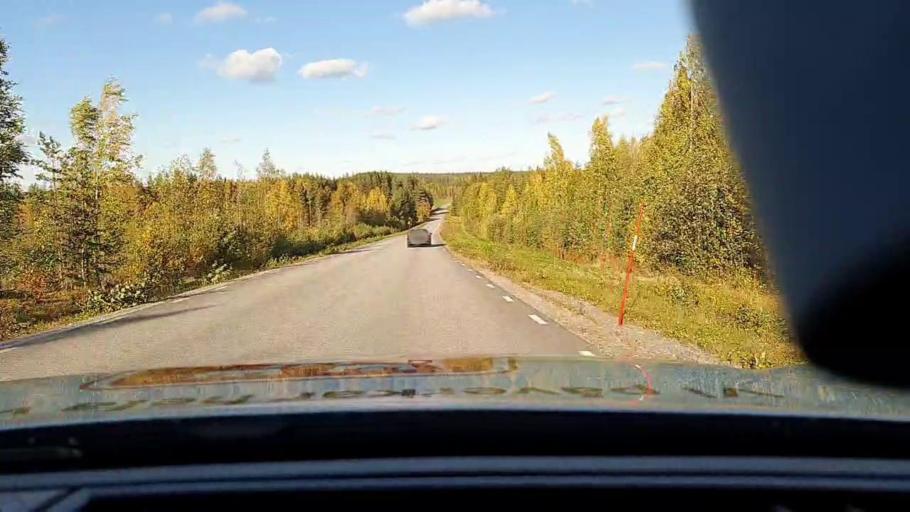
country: SE
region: Norrbotten
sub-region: Pitea Kommun
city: Norrfjarden
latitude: 65.5065
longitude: 21.4822
